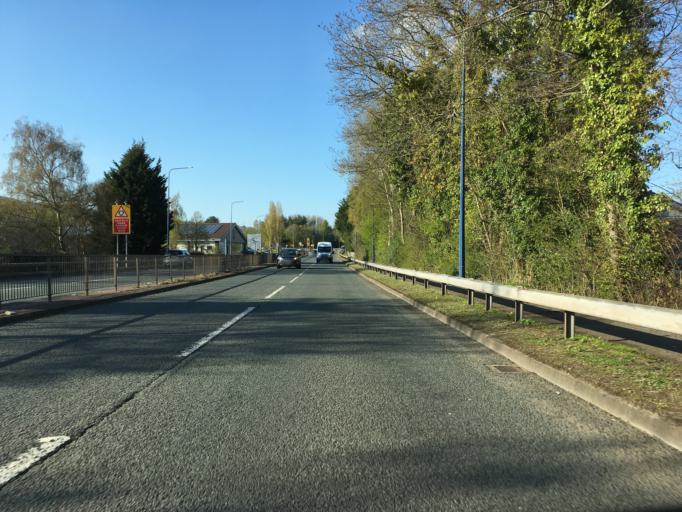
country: GB
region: Wales
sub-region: Torfaen County Borough
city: Cwmbran
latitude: 51.6538
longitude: -3.0260
